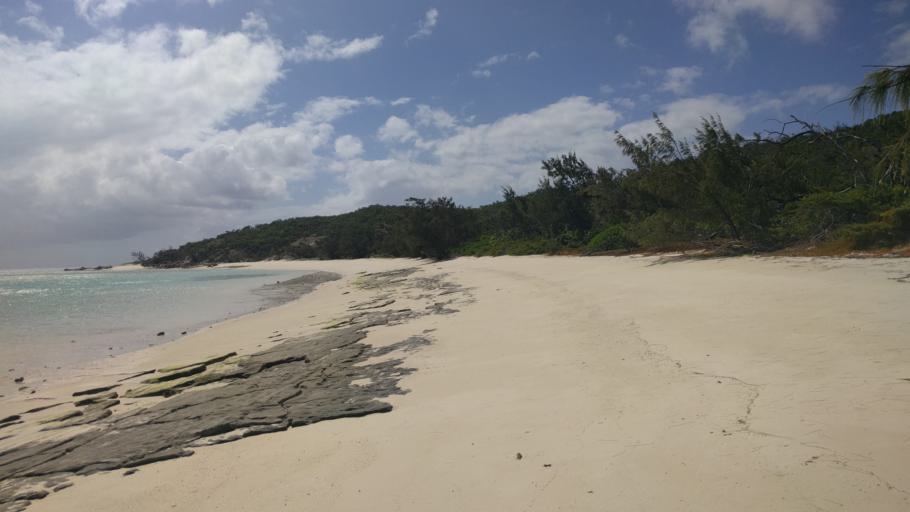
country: AU
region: Queensland
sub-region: Cook
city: Cooktown
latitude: -14.6763
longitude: 145.4470
